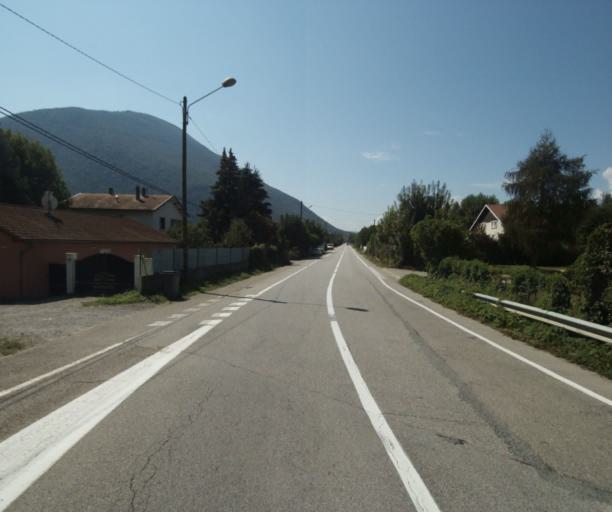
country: FR
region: Rhone-Alpes
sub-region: Departement de l'Isere
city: Champ-sur-Drac
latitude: 45.0828
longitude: 5.7281
